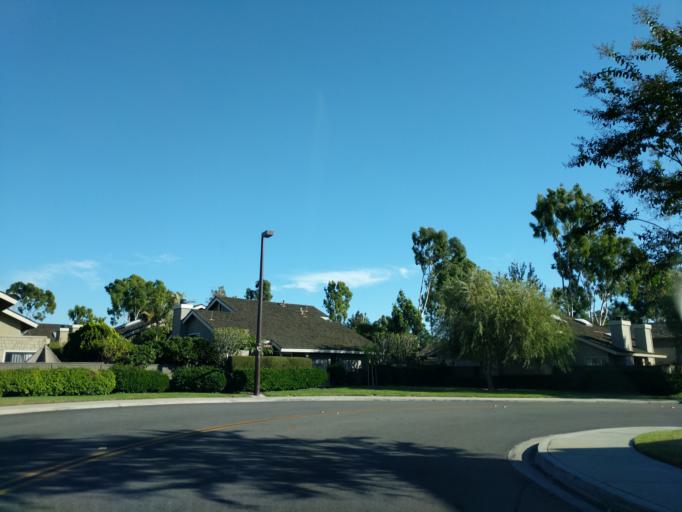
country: US
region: California
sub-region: Orange County
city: Irvine
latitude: 33.6813
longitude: -117.7999
